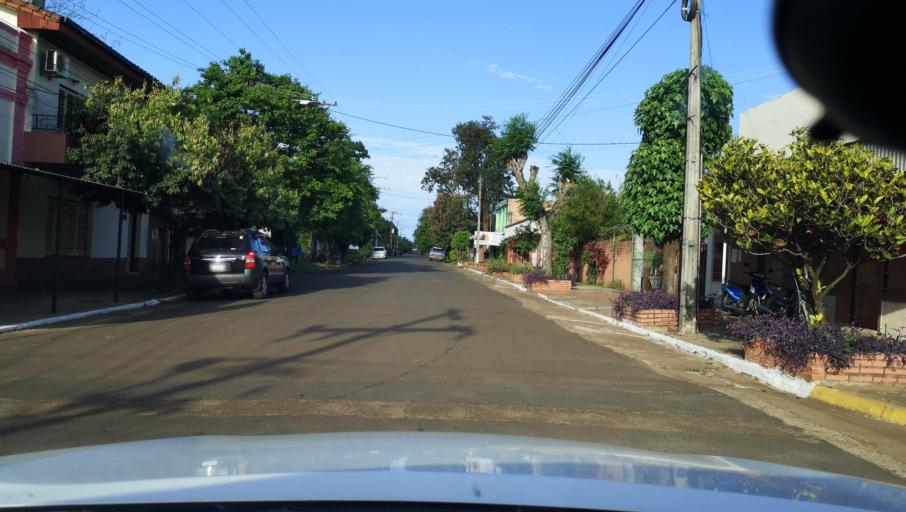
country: PY
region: Itapua
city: Carmen del Parana
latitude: -27.1601
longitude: -56.2391
